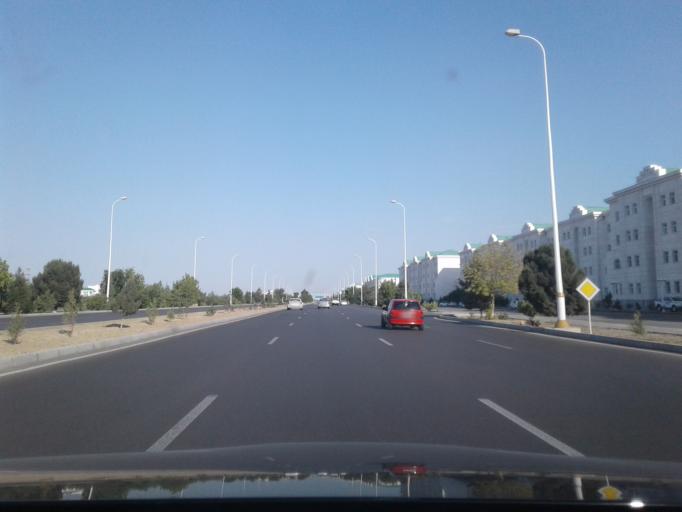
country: TM
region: Ahal
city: Ashgabat
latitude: 37.9924
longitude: 58.3156
